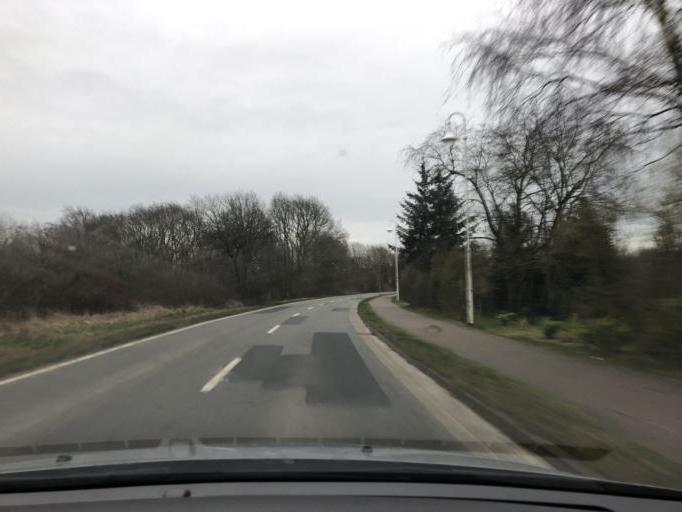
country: DE
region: Mecklenburg-Vorpommern
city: Zingst
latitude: 54.4392
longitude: 12.6732
